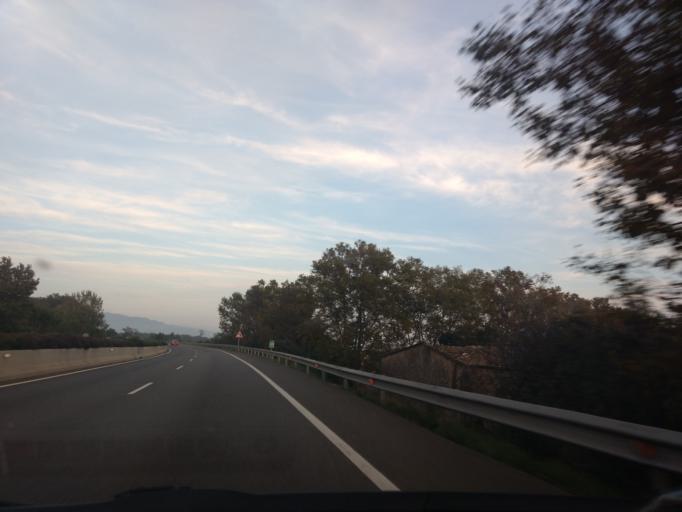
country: ES
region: Catalonia
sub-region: Provincia de Girona
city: Castello d'Empuries
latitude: 42.2514
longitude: 3.0788
